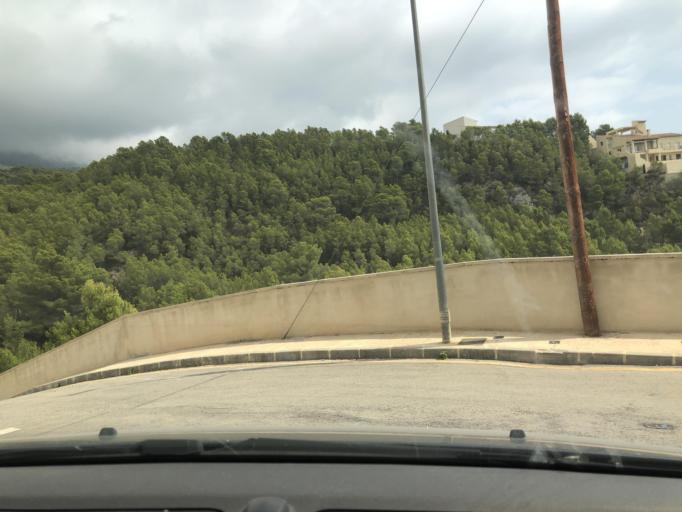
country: ES
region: Valencia
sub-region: Provincia de Alicante
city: Callosa d'En Sarria
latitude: 38.6423
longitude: -0.0710
